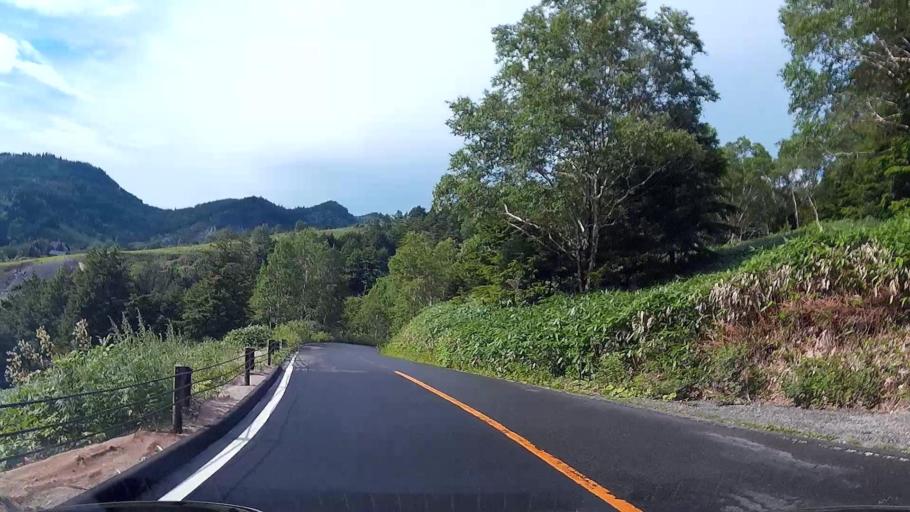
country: JP
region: Nagano
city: Nakano
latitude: 36.6363
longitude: 138.5136
